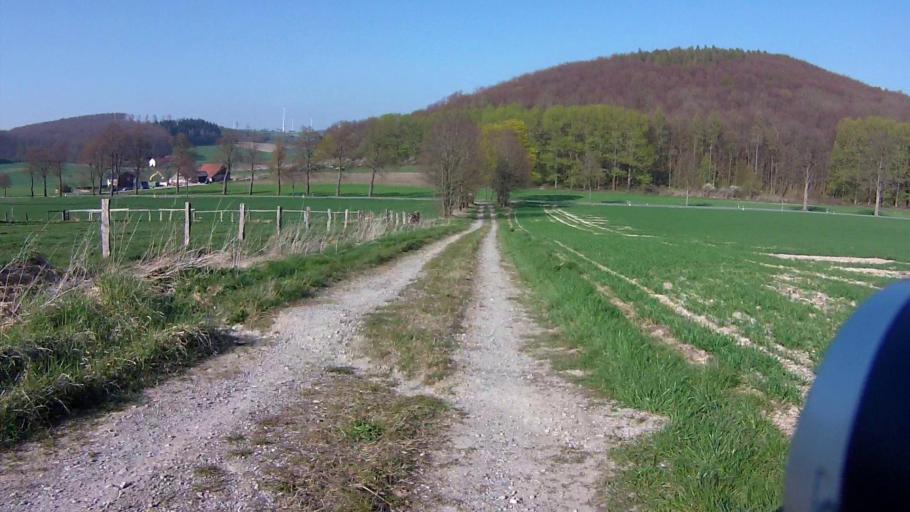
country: DE
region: North Rhine-Westphalia
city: Lichtenau
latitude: 51.6907
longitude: 8.8883
